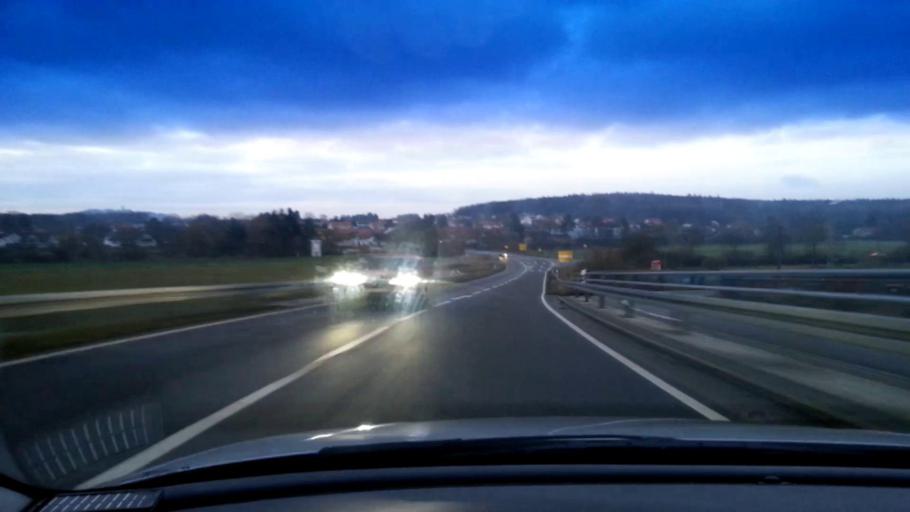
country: DE
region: Bavaria
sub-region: Upper Franconia
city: Frensdorf
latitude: 49.8487
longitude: 10.8775
